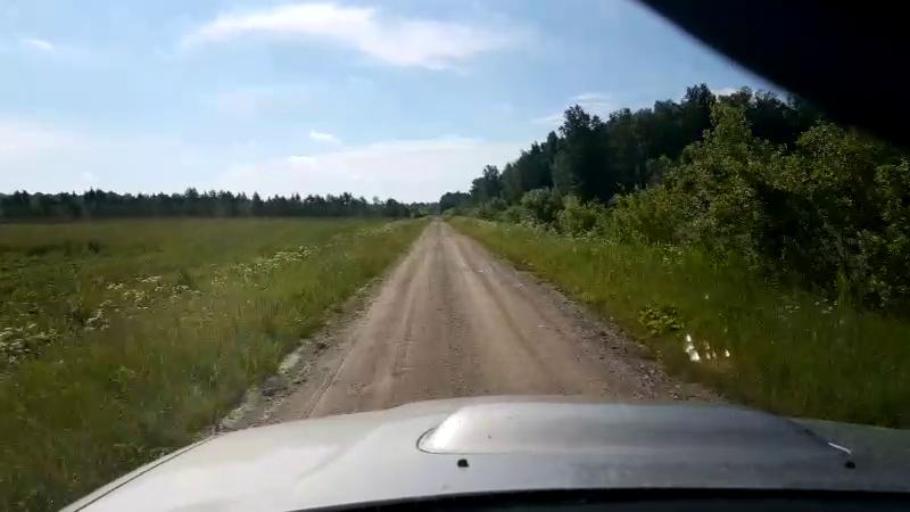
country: EE
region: Paernumaa
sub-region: Sindi linn
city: Sindi
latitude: 58.4967
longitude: 24.6597
